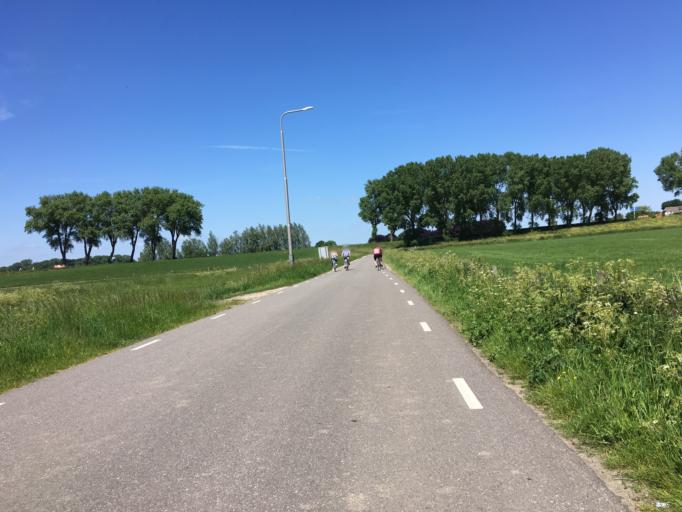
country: NL
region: Gelderland
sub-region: Gemeente Zaltbommel
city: Nederhemert-Noord
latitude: 51.7445
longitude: 5.1632
